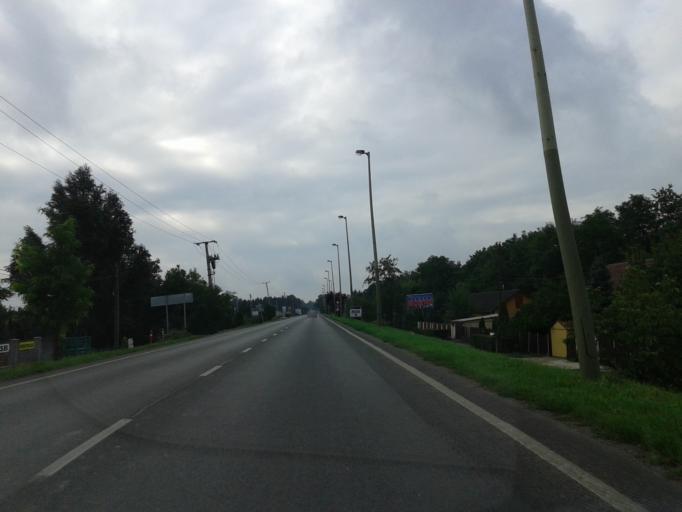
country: HU
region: Csongrad
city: Szeged
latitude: 46.2405
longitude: 20.1655
